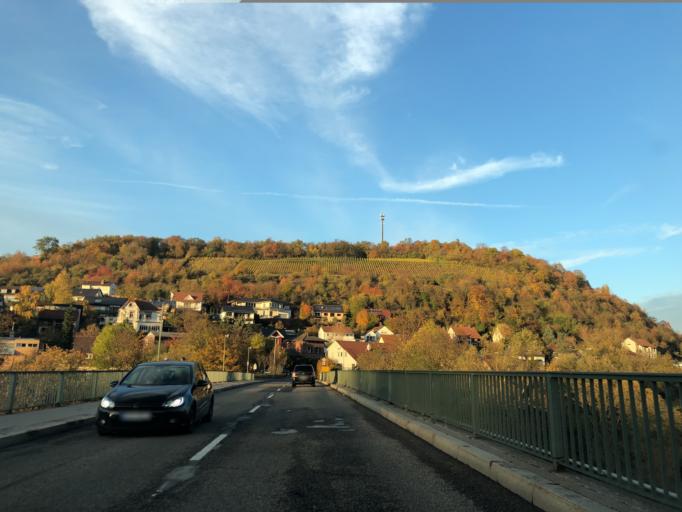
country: DE
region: Bavaria
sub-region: Regierungsbezirk Unterfranken
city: Kreuzwertheim
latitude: 49.7612
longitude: 9.5244
